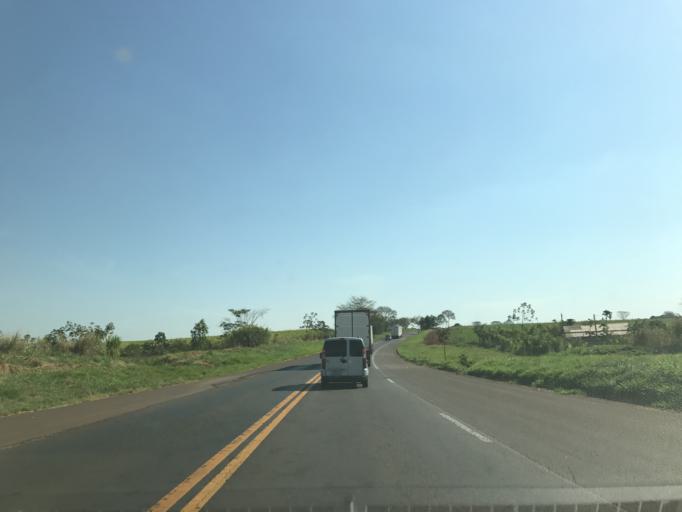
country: BR
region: Sao Paulo
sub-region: Penapolis
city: Penapolis
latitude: -21.4830
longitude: -50.2066
